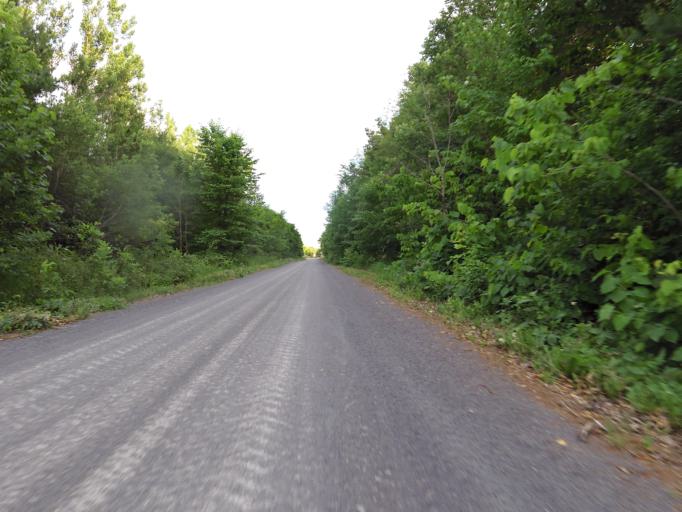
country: CA
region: Ontario
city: Arnprior
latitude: 45.3358
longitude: -76.2955
